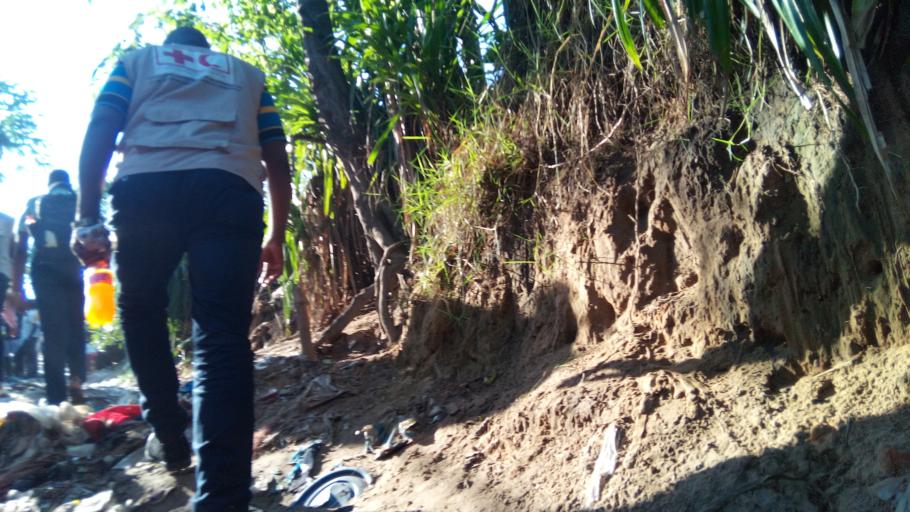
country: CD
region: Kinshasa
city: Kinshasa
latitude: -4.3690
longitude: 15.2764
